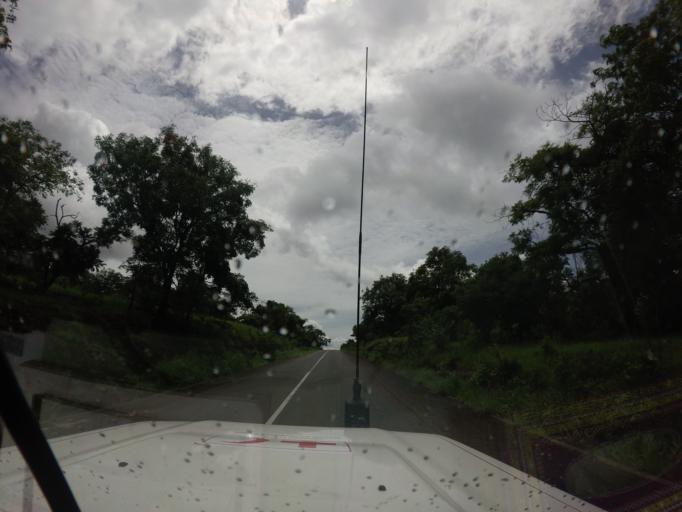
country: GN
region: Faranah
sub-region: Faranah Prefecture
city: Faranah
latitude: 10.0280
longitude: -10.9787
